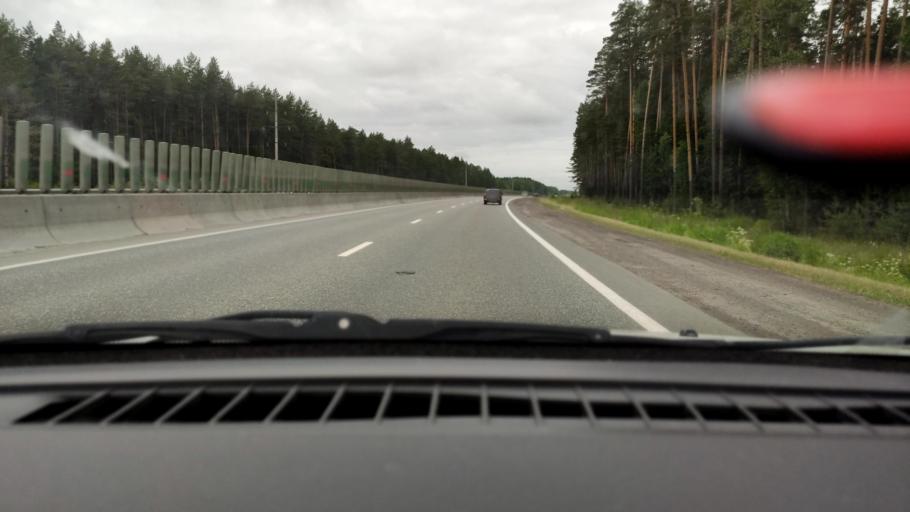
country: RU
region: Perm
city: Overyata
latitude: 58.0375
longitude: 55.9857
